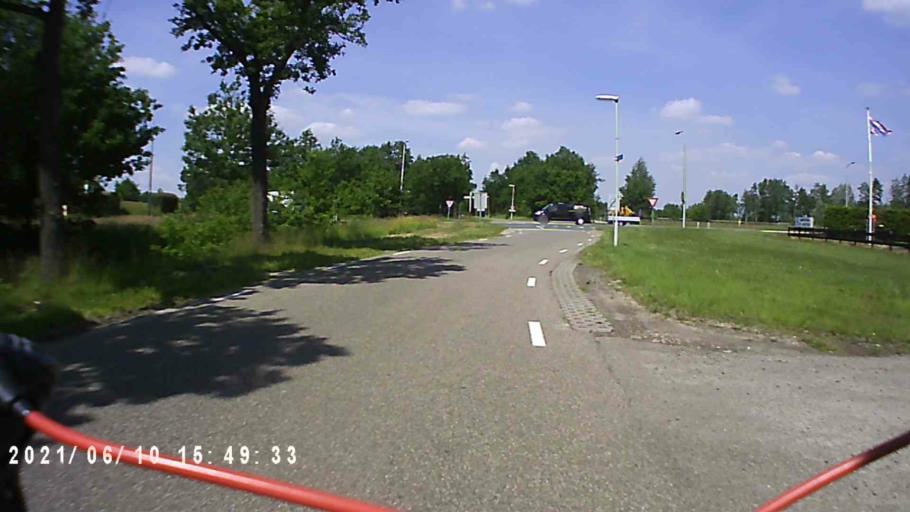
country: NL
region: Friesland
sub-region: Gemeente Achtkarspelen
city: Harkema
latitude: 53.1687
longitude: 6.1196
